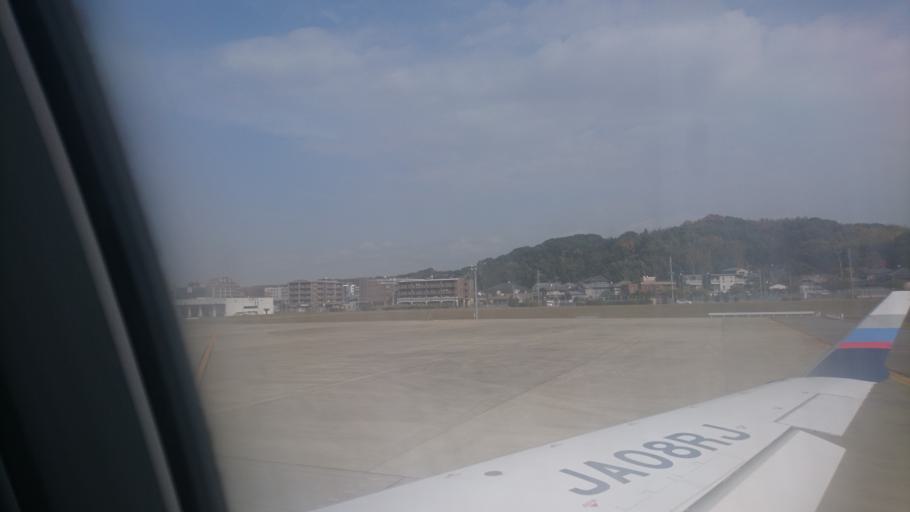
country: JP
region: Fukuoka
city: Fukuoka-shi
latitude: 33.5837
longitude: 130.4545
